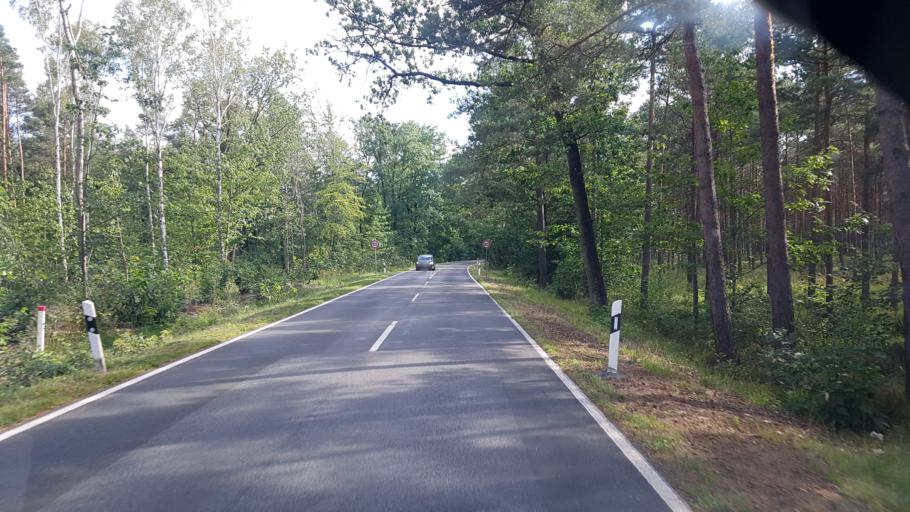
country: DE
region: Saxony
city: Gross Duben
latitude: 51.5879
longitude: 14.5720
